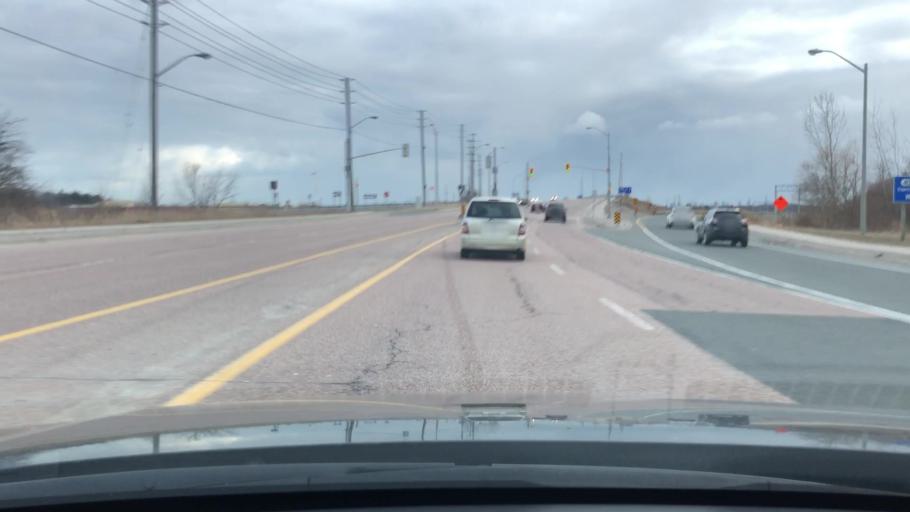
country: CA
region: Ontario
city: Markham
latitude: 43.8733
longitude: -79.2336
